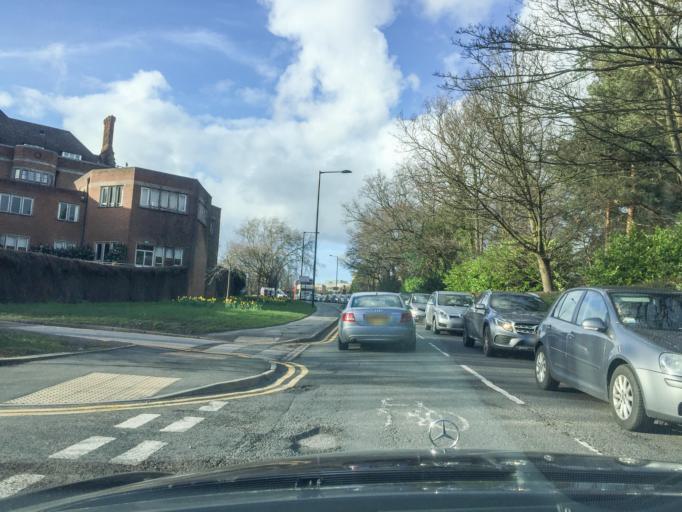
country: GB
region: England
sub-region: City and Borough of Birmingham
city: Birmingham
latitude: 52.4488
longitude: -1.9260
